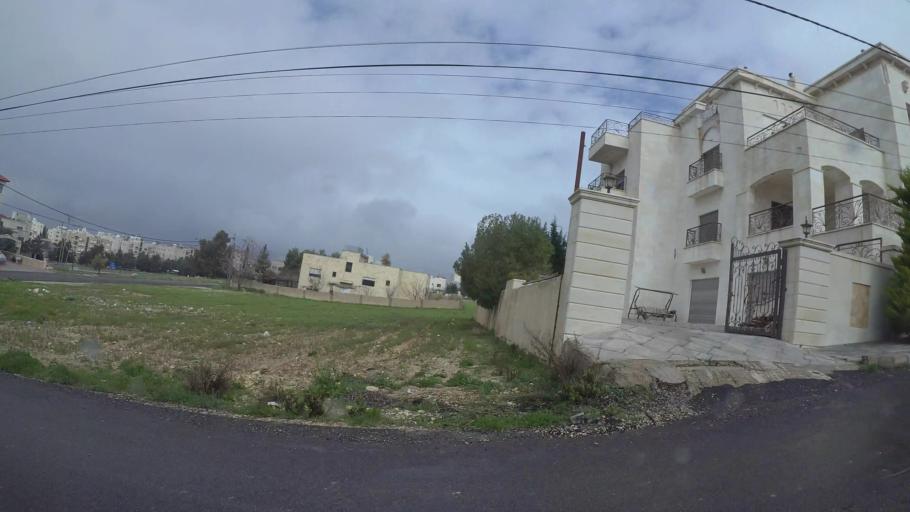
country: JO
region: Amman
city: Al Jubayhah
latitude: 32.0265
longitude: 35.8239
